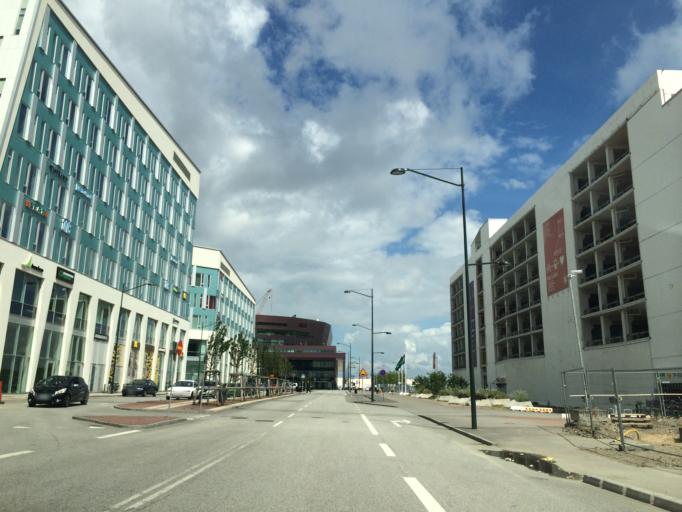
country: SE
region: Skane
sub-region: Malmo
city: Bunkeflostrand
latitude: 55.5620
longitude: 12.9768
